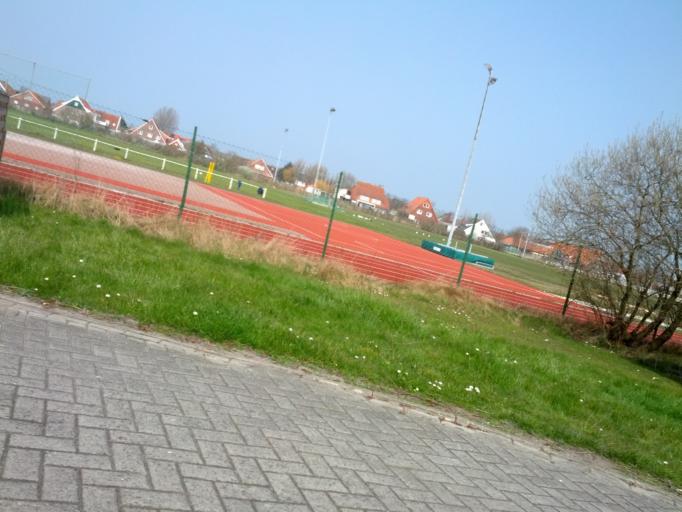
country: DE
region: Lower Saxony
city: Langeoog
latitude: 53.7430
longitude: 7.4913
